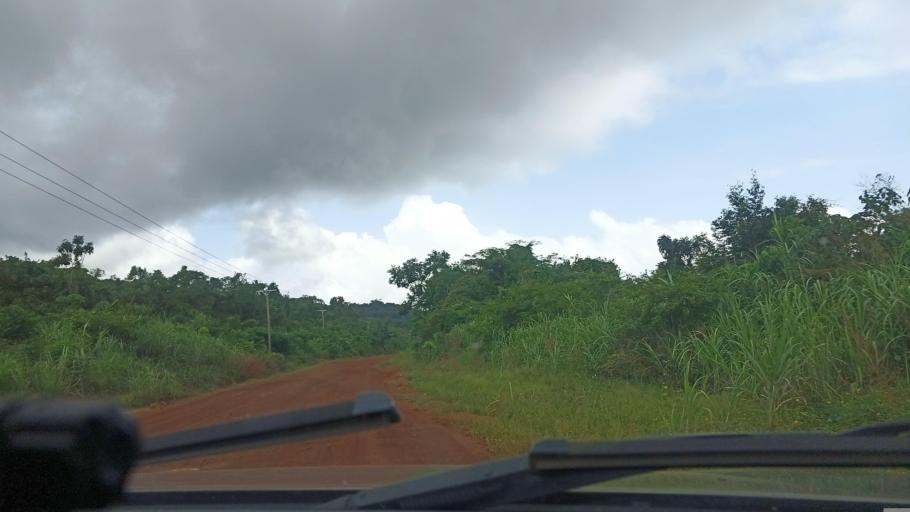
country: LR
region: Grand Cape Mount
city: Robertsport
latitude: 6.7093
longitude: -11.3348
